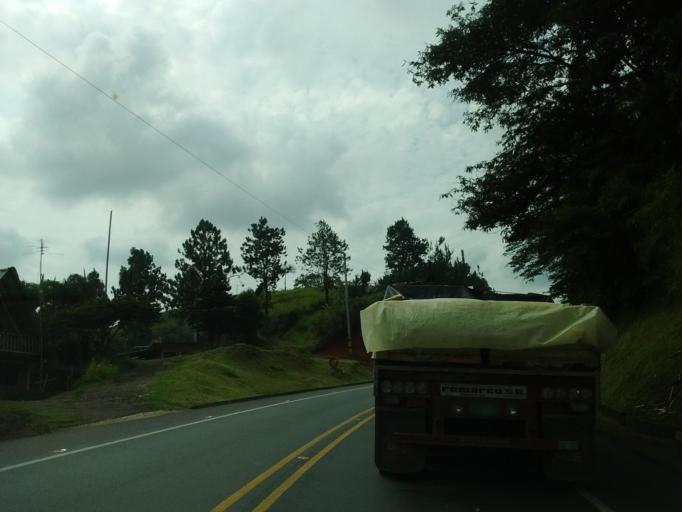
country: CO
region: Cauca
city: Caldono
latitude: 2.7874
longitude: -76.5519
